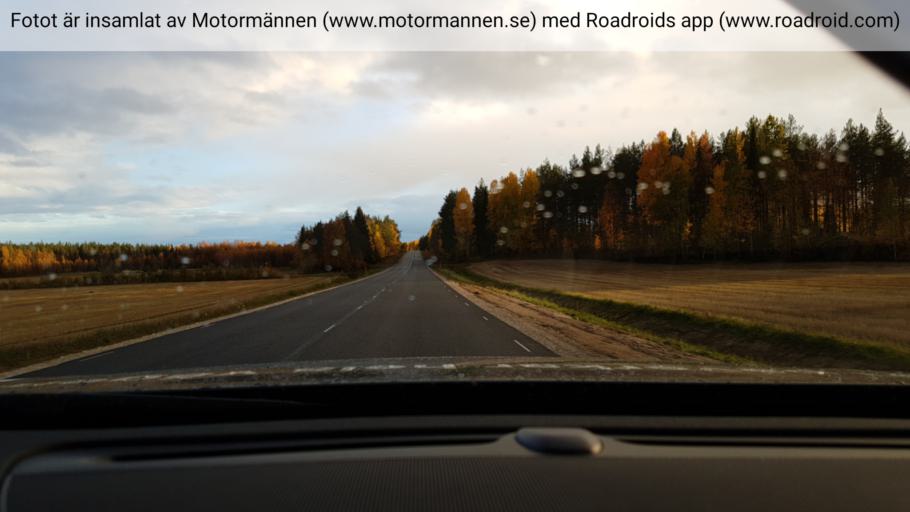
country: SE
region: Norrbotten
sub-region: Overkalix Kommun
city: OEverkalix
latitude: 66.4524
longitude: 22.7882
